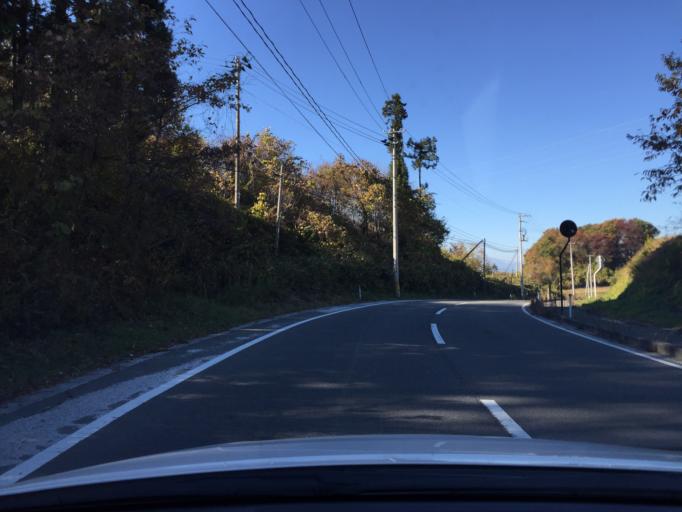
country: JP
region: Fukushima
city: Miharu
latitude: 37.4300
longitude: 140.5158
